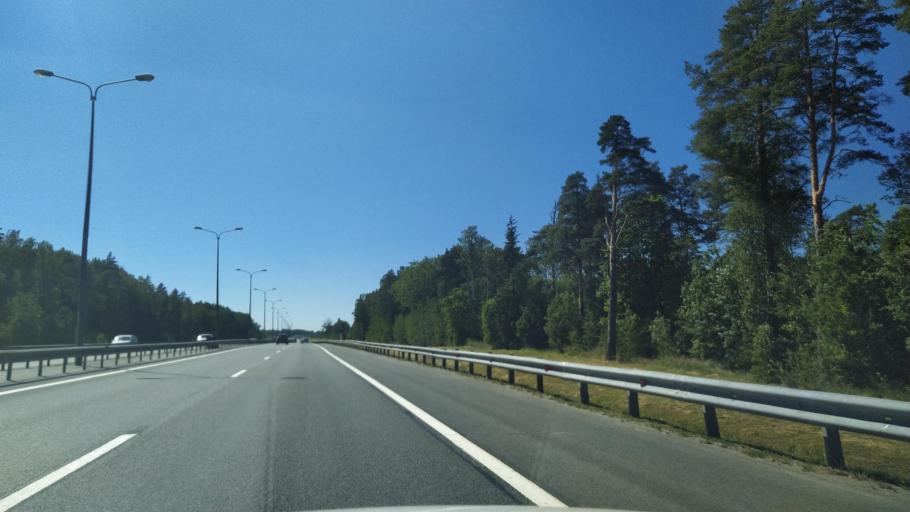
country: RU
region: St.-Petersburg
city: Lisiy Nos
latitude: 60.0447
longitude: 30.0340
